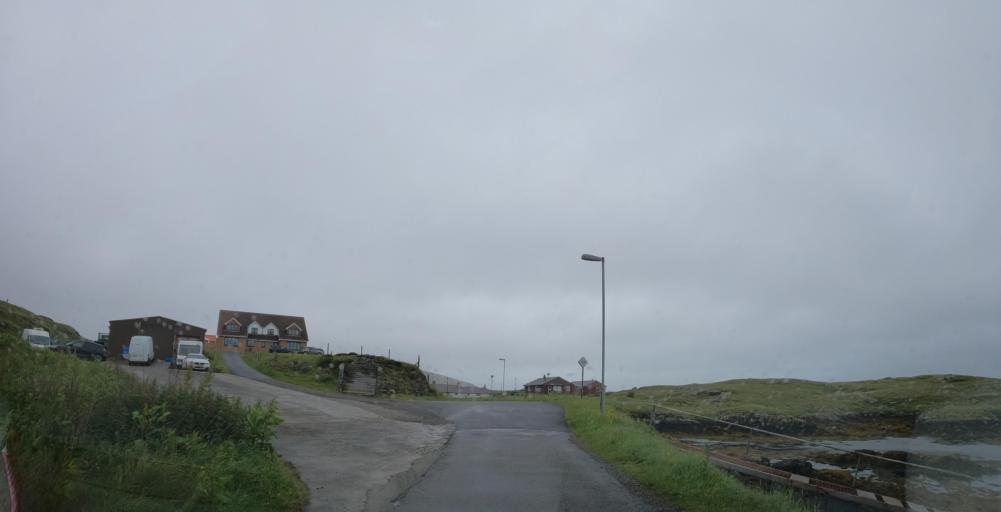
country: GB
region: Scotland
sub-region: Eilean Siar
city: Barra
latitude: 56.9989
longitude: -7.4203
